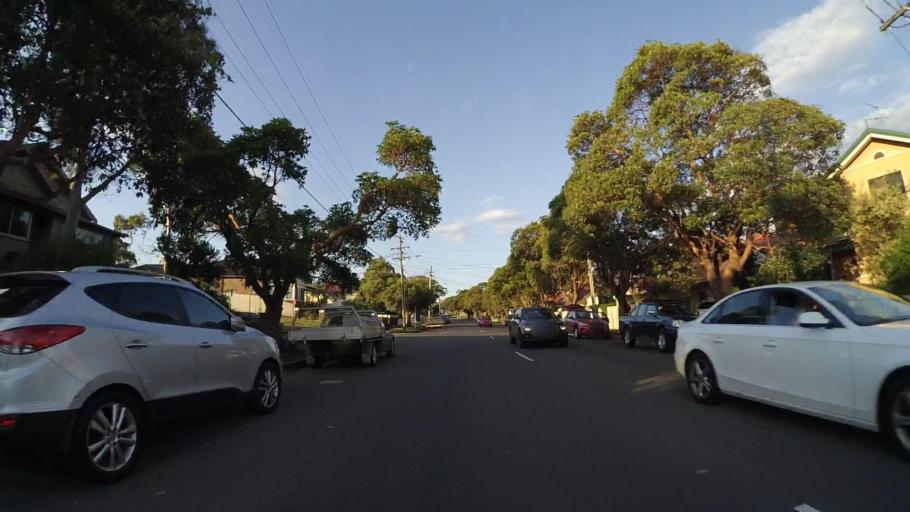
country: AU
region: New South Wales
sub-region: Randwick
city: Daceyville
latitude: -33.9298
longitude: 151.2322
